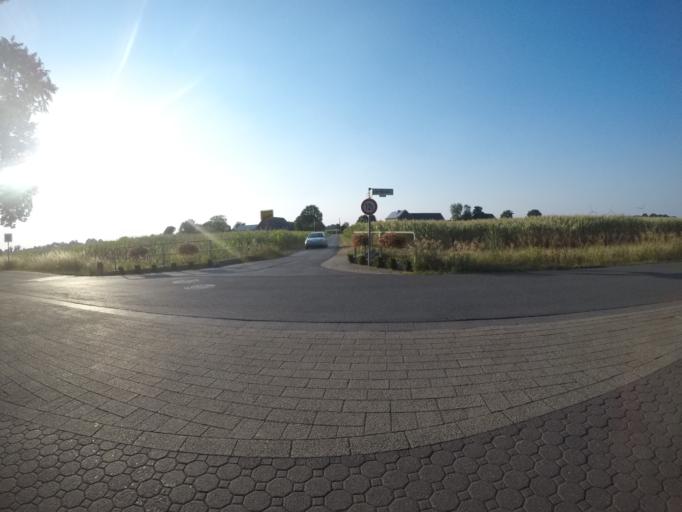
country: DE
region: North Rhine-Westphalia
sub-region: Regierungsbezirk Dusseldorf
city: Bocholt
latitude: 51.8644
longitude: 6.5628
